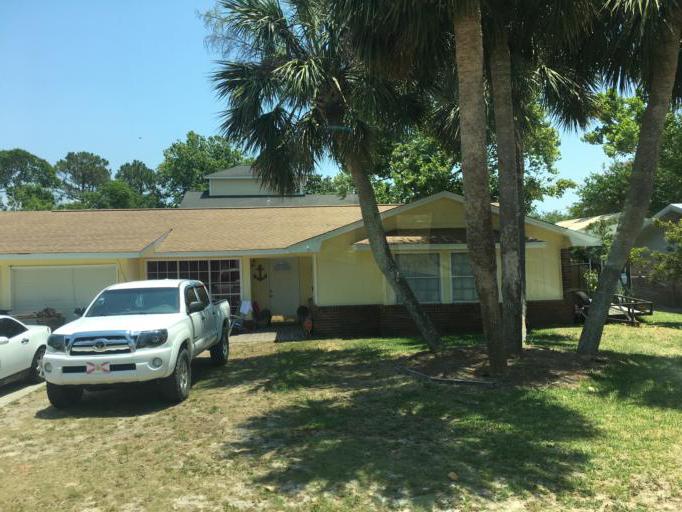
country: US
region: Florida
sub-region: Bay County
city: Panama City Beach
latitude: 30.2101
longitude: -85.8578
